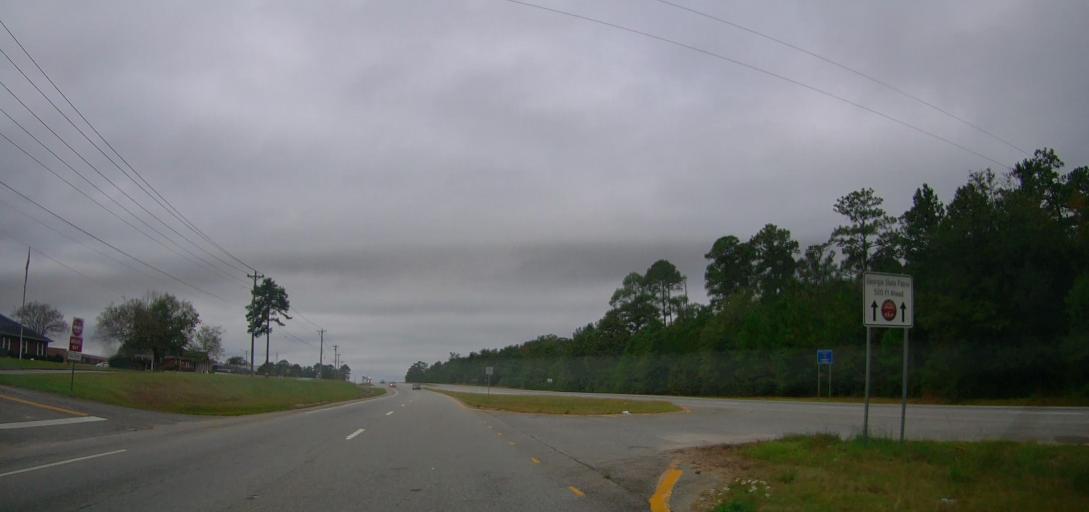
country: US
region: Georgia
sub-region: Thomas County
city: Thomasville
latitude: 30.8745
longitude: -83.9621
